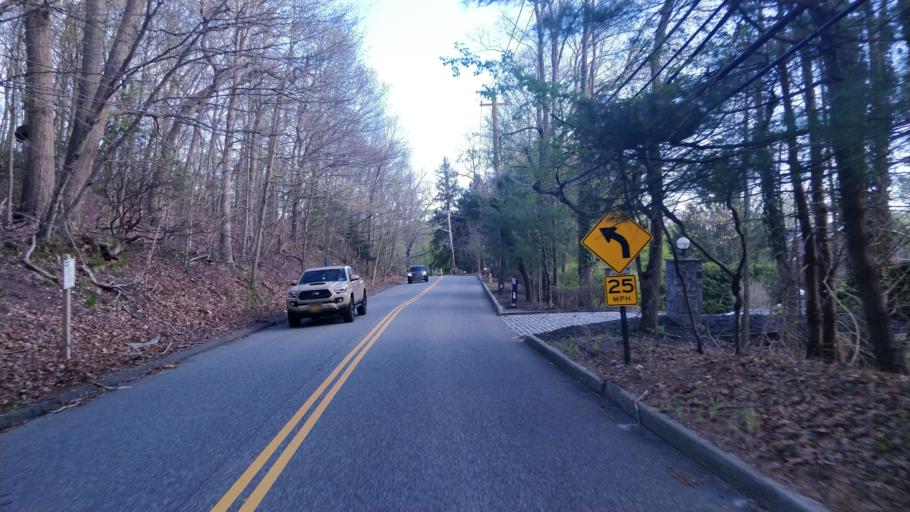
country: US
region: New York
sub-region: Suffolk County
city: Village of the Branch
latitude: 40.8717
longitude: -73.1911
